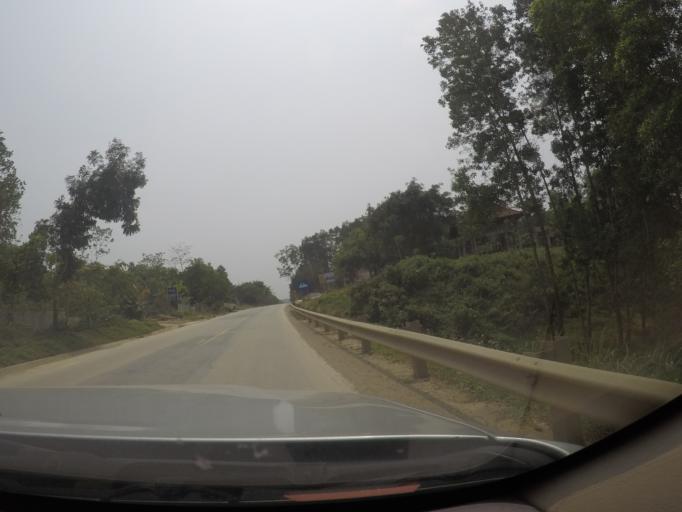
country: VN
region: Thanh Hoa
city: Thi Tran Thuong Xuan
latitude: 19.8117
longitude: 105.3948
